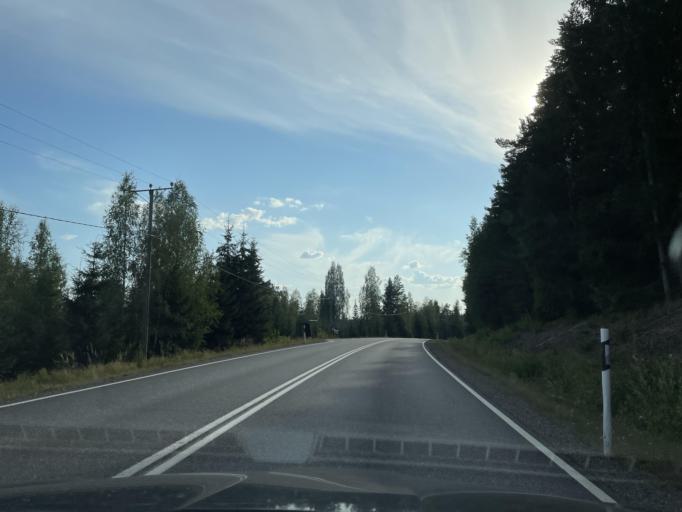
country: FI
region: Paijanne Tavastia
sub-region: Lahti
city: Auttoinen
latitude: 61.3209
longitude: 25.1590
